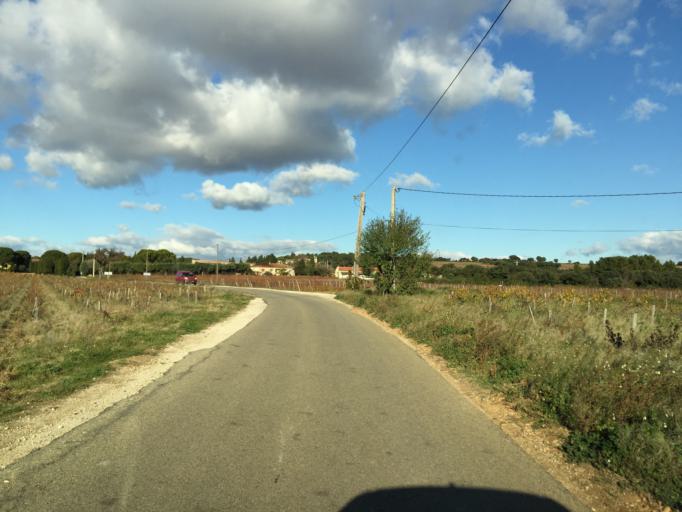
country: FR
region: Provence-Alpes-Cote d'Azur
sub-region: Departement du Vaucluse
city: Chateauneuf-du-Pape
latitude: 44.0455
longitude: 4.8360
